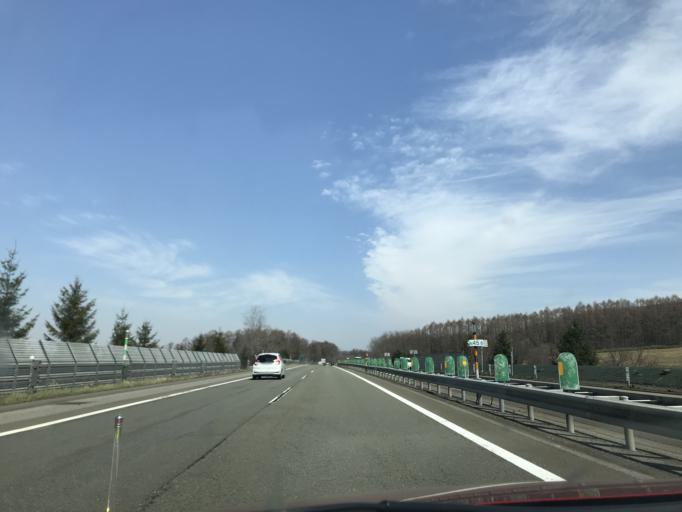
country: JP
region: Hokkaido
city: Bibai
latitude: 43.2740
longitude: 141.8493
